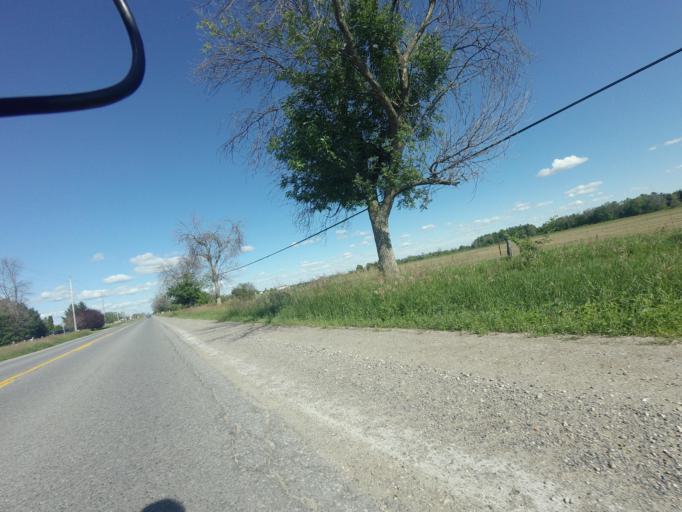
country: CA
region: Ontario
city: Arnprior
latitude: 45.4166
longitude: -76.4115
